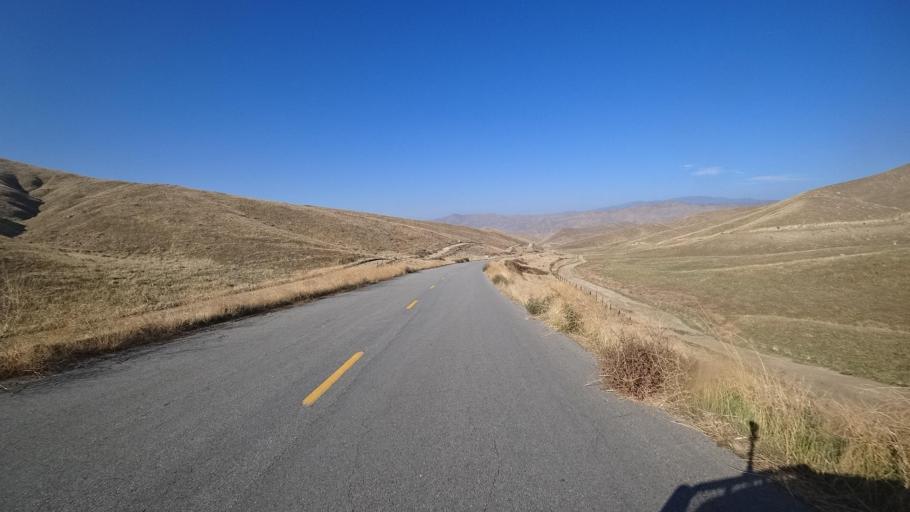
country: US
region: California
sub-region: Kern County
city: Bear Valley Springs
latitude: 35.2807
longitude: -118.6955
